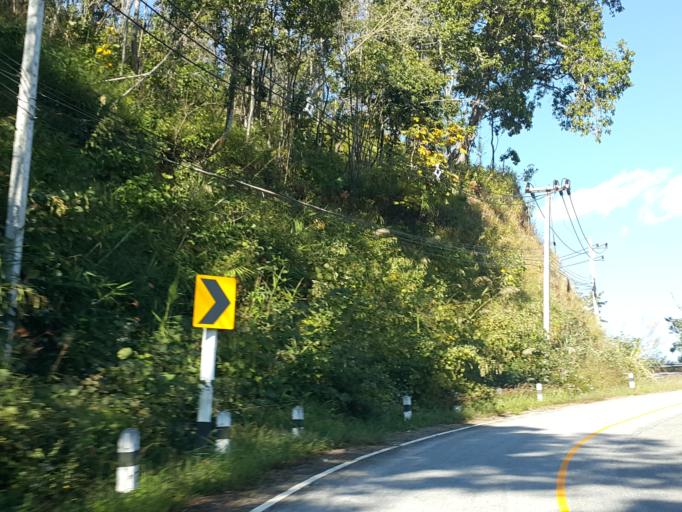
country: TH
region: Chiang Mai
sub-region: Amphoe Chiang Dao
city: Chiang Dao
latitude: 19.5281
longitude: 98.8774
